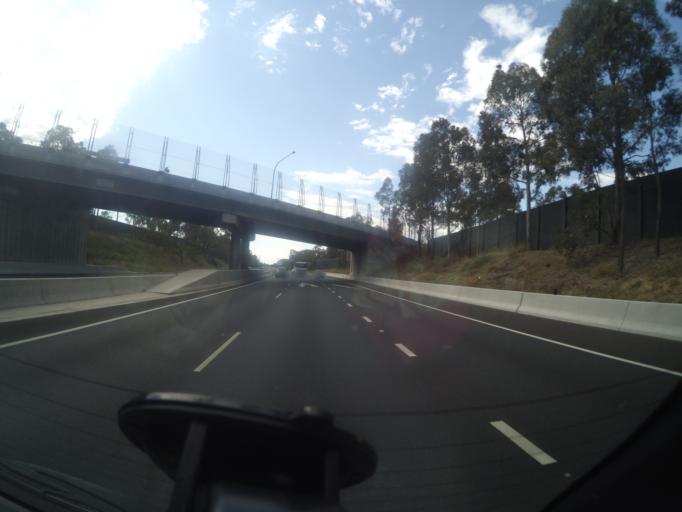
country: AU
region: New South Wales
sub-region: Campbelltown Municipality
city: Glenfield
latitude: -33.9465
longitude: 150.8957
